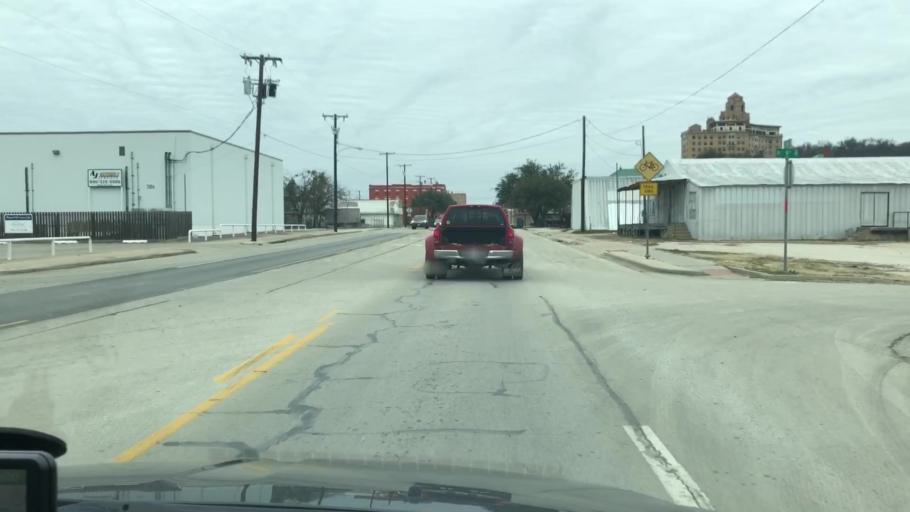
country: US
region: Texas
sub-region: Palo Pinto County
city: Mineral Wells
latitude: 32.8055
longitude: -98.1129
